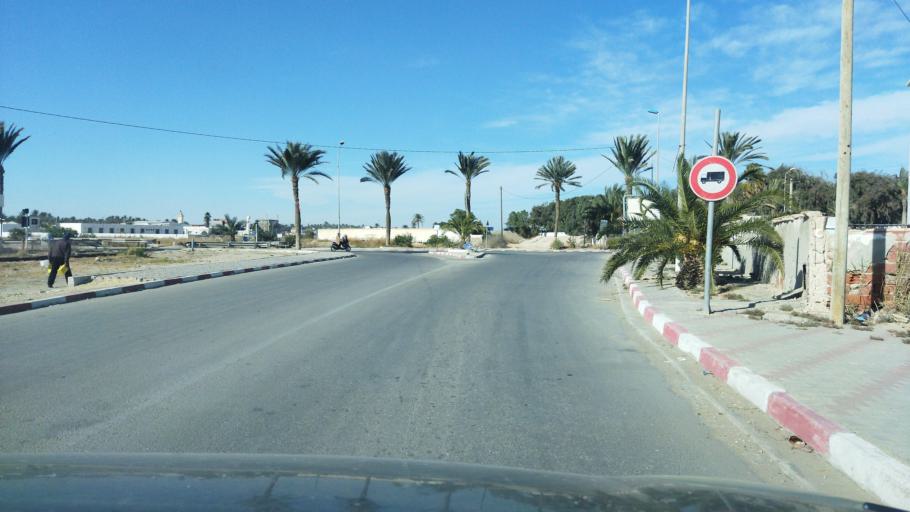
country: TN
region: Qabis
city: Gabes
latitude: 33.8905
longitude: 10.1139
